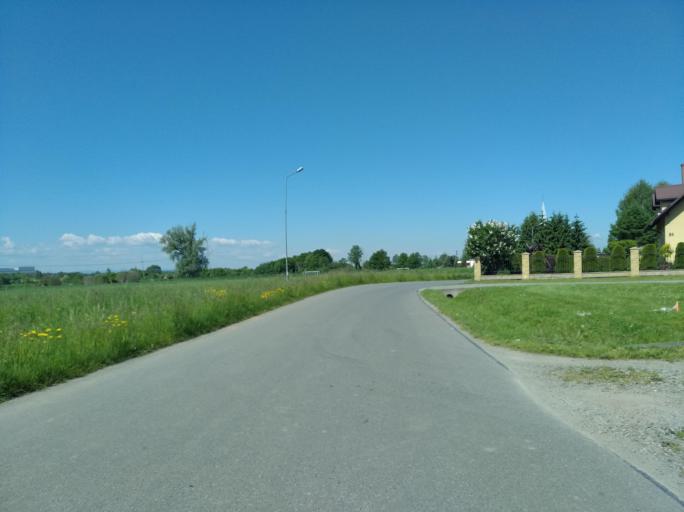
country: PL
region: Subcarpathian Voivodeship
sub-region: Krosno
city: Krosno
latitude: 49.7198
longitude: 21.7740
